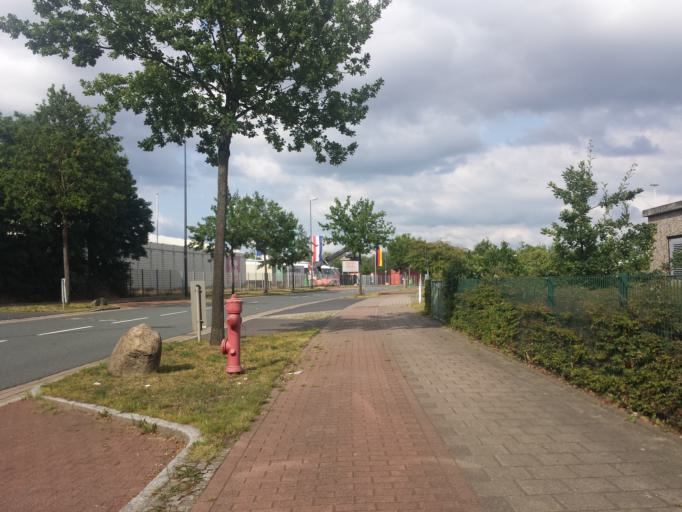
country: DE
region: Lower Saxony
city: Stuhr
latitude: 53.0931
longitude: 8.7065
